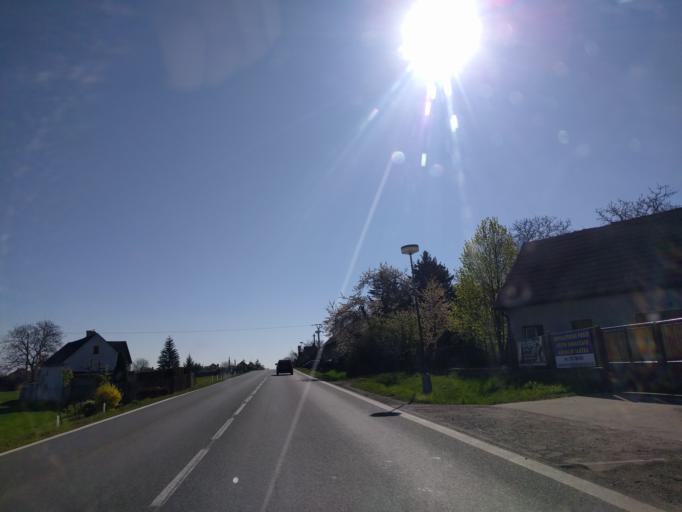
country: CZ
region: Central Bohemia
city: Mukarov
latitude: 49.9874
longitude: 14.7814
